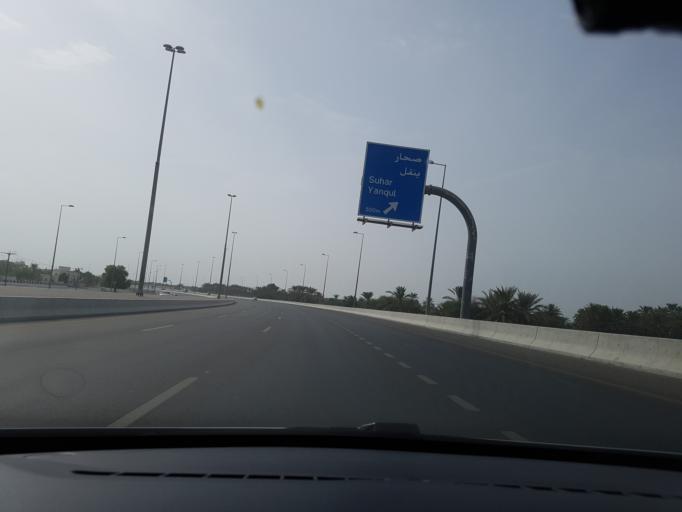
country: OM
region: Al Batinah
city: Al Sohar
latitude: 24.3476
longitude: 56.7171
